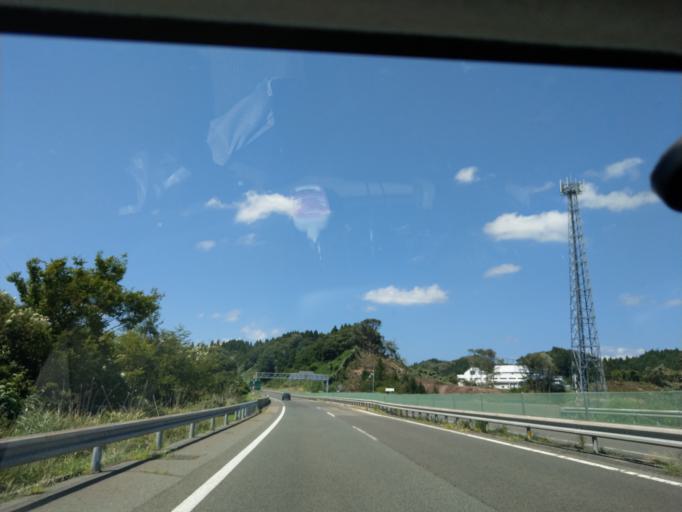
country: JP
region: Akita
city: Akita
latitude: 39.6514
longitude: 140.2053
